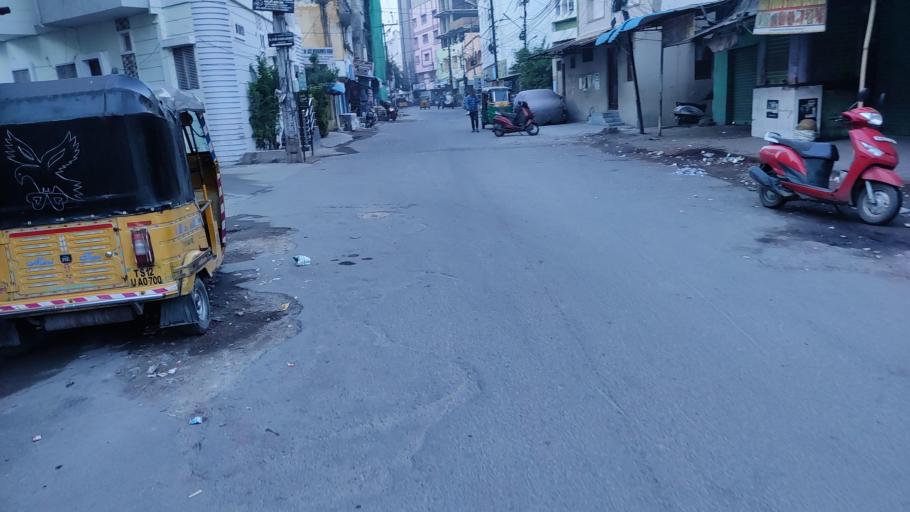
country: IN
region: Telangana
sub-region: Rangareddi
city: Gaddi Annaram
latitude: 17.3702
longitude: 78.4917
